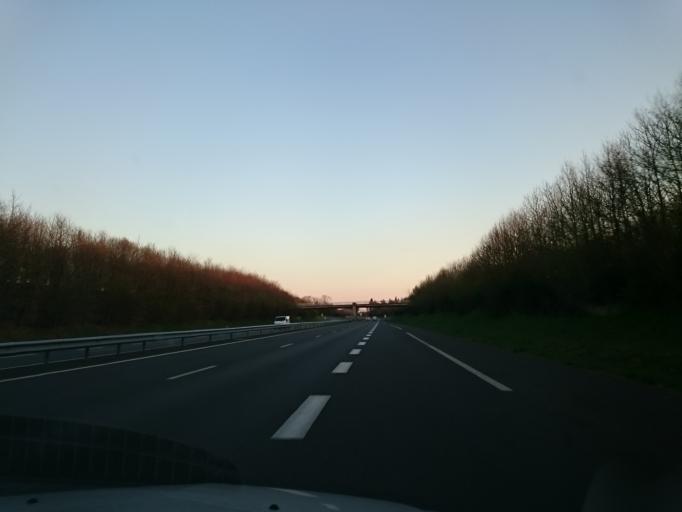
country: FR
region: Brittany
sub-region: Departement d'Ille-et-Vilaine
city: Saint-Etienne-en-Cogles
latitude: 48.4417
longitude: -1.3235
